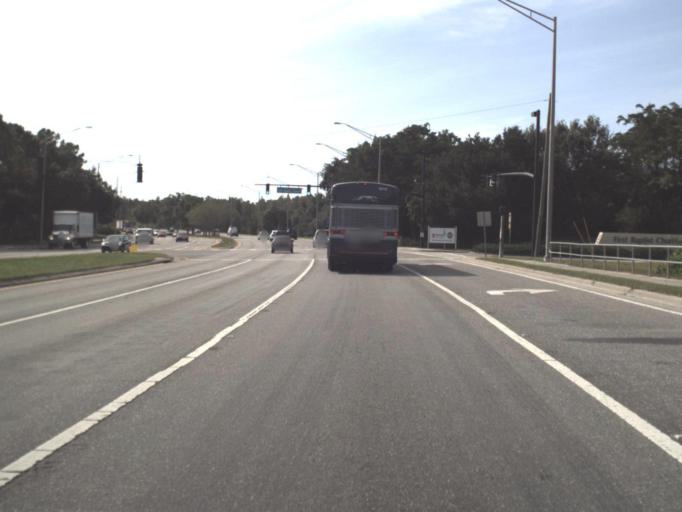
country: US
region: Florida
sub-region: Orange County
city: Holden Heights
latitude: 28.5163
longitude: -81.4203
